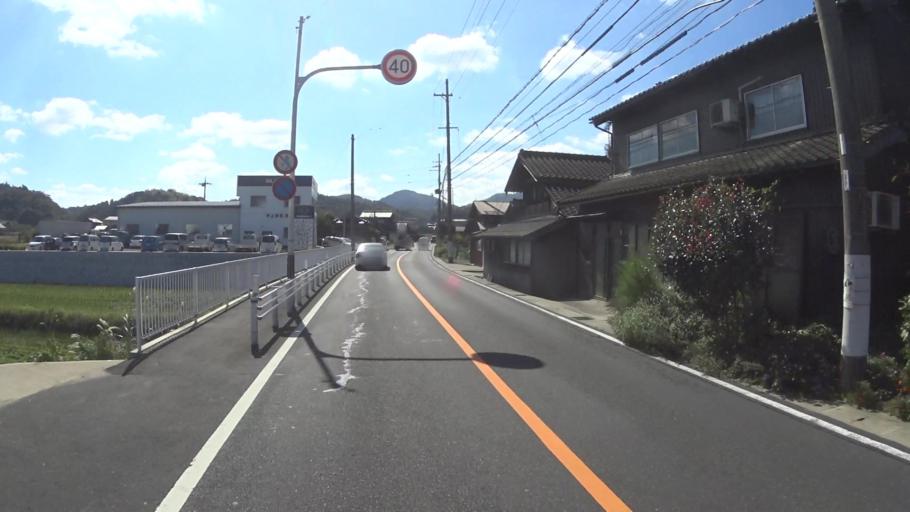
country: JP
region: Kyoto
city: Miyazu
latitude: 35.6564
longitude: 135.0326
